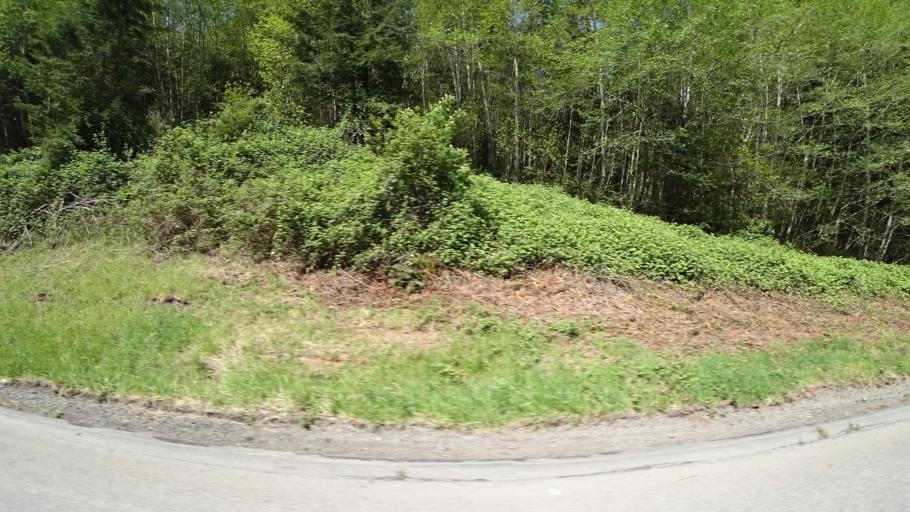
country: US
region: California
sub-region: Del Norte County
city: Bertsch-Oceanview
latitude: 41.4390
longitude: -124.0219
